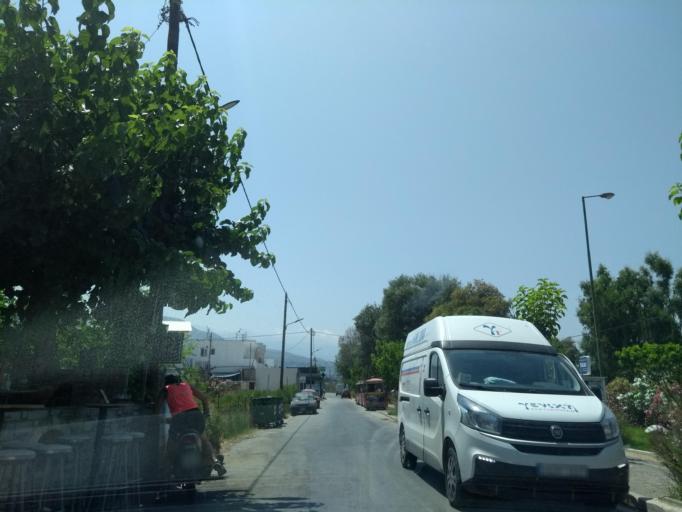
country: GR
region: Crete
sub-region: Nomos Chanias
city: Georgioupolis
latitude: 35.3511
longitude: 24.2978
